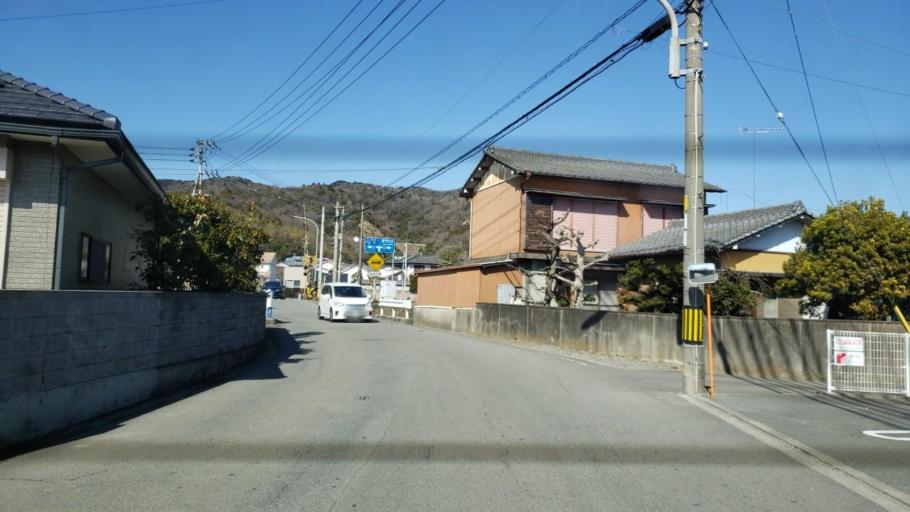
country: JP
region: Tokushima
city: Narutocho-mitsuishi
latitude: 34.1550
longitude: 134.5317
